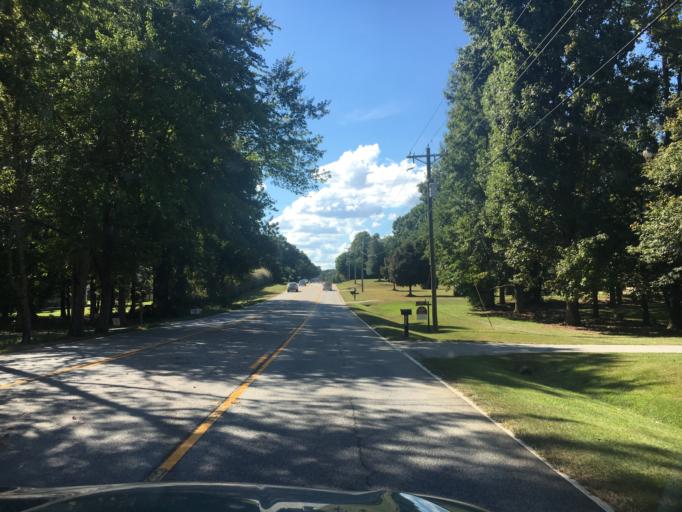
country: US
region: South Carolina
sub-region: Greenville County
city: Five Forks
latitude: 34.8239
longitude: -82.2337
